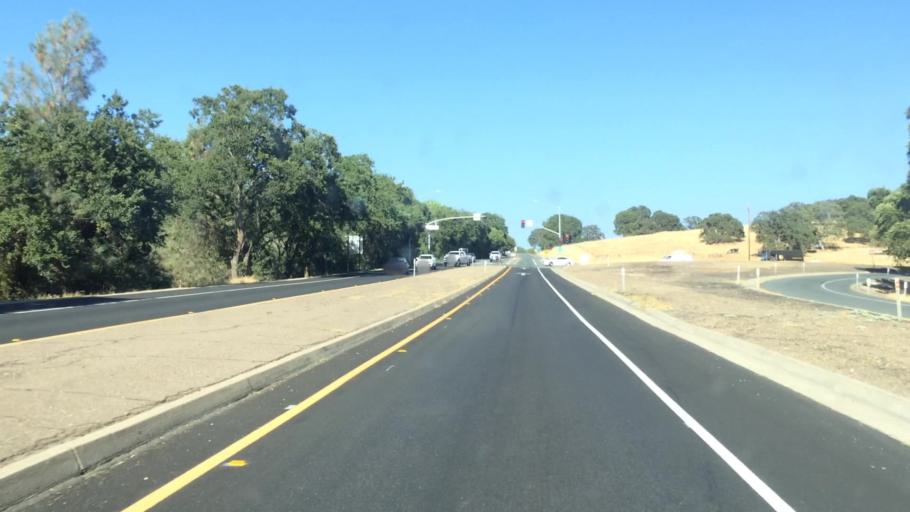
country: US
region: California
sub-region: Amador County
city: Plymouth
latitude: 38.4538
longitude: -120.8695
